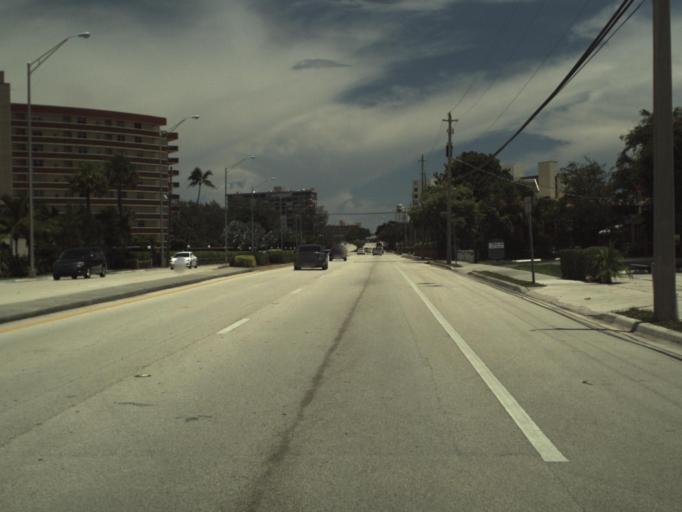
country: US
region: Florida
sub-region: Broward County
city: Lighthouse Point
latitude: 26.2501
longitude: -80.0955
